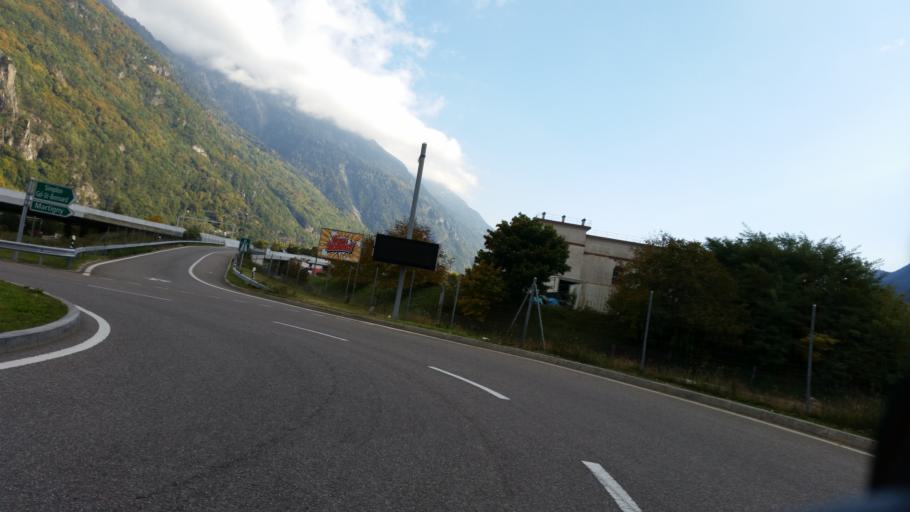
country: CH
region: Valais
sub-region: Saint-Maurice District
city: Saint-Maurice
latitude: 46.2042
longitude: 7.0111
